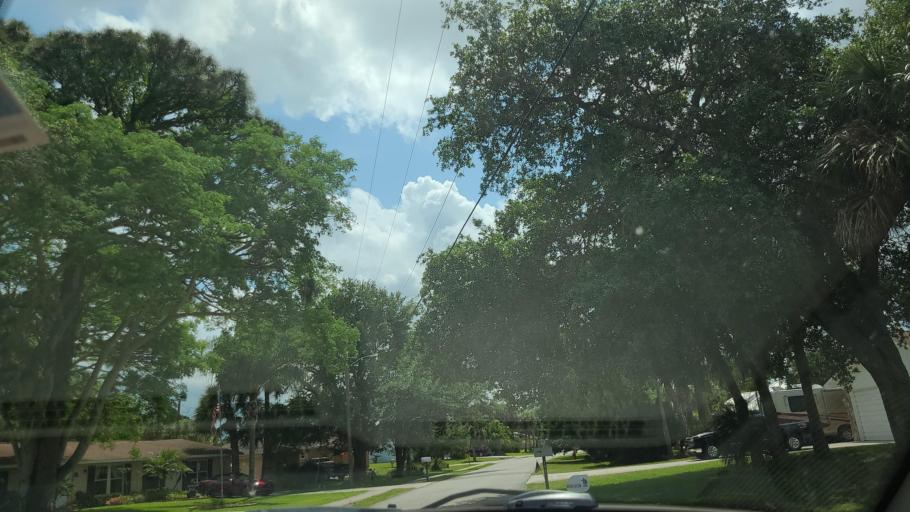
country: US
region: Florida
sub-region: Indian River County
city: Sebastian
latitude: 27.8023
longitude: -80.4940
